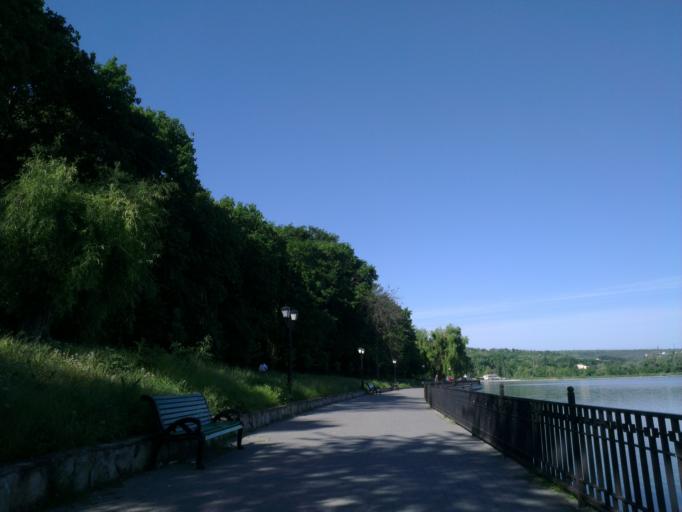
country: MD
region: Chisinau
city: Chisinau
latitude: 47.0173
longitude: 28.8162
